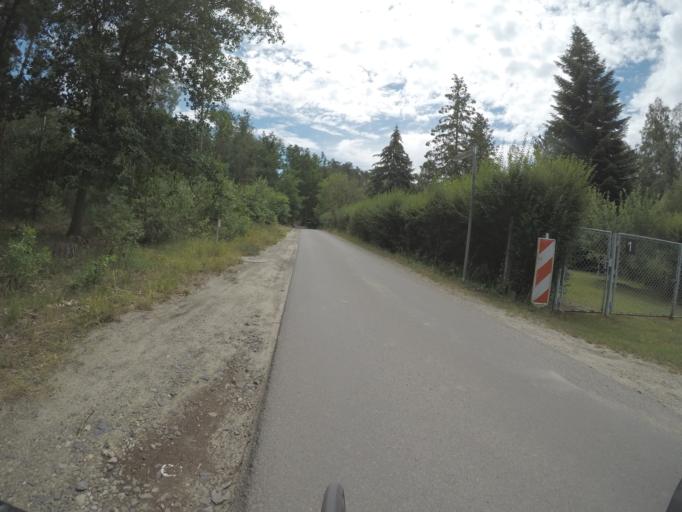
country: DE
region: Brandenburg
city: Storkow
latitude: 52.2396
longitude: 13.9601
